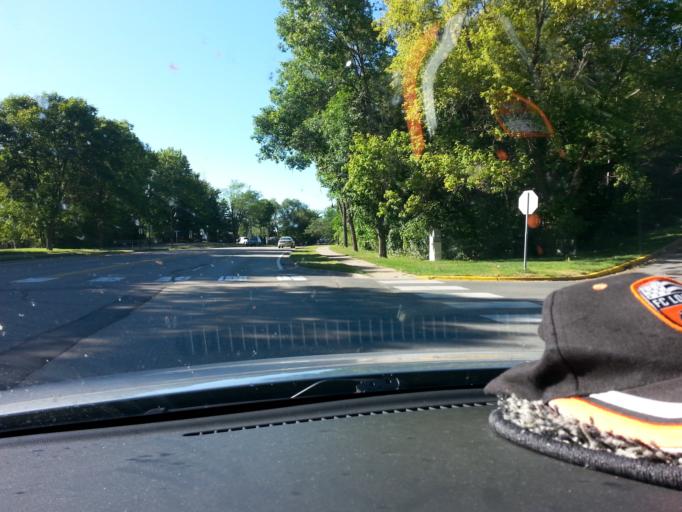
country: US
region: Minnesota
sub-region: Scott County
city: Prior Lake
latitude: 44.7157
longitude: -93.4325
